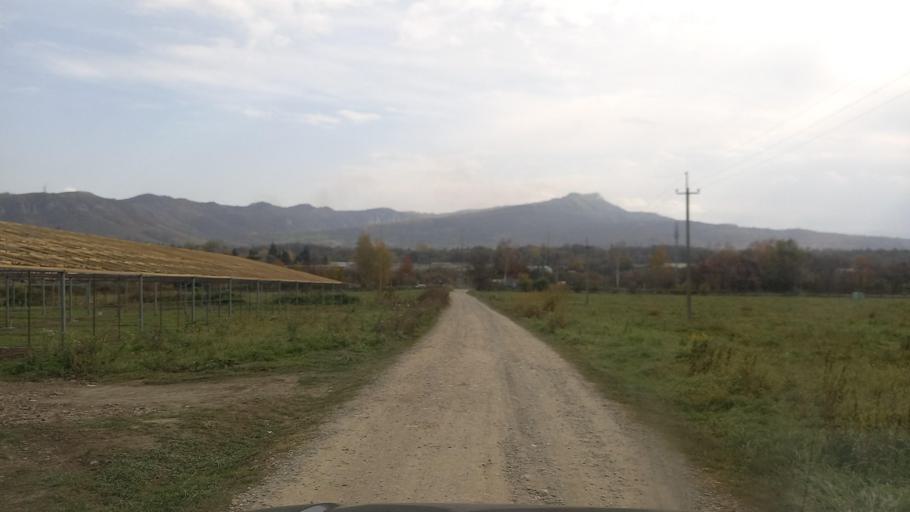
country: RU
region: Krasnodarskiy
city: Psebay
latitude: 44.1486
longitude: 40.8260
